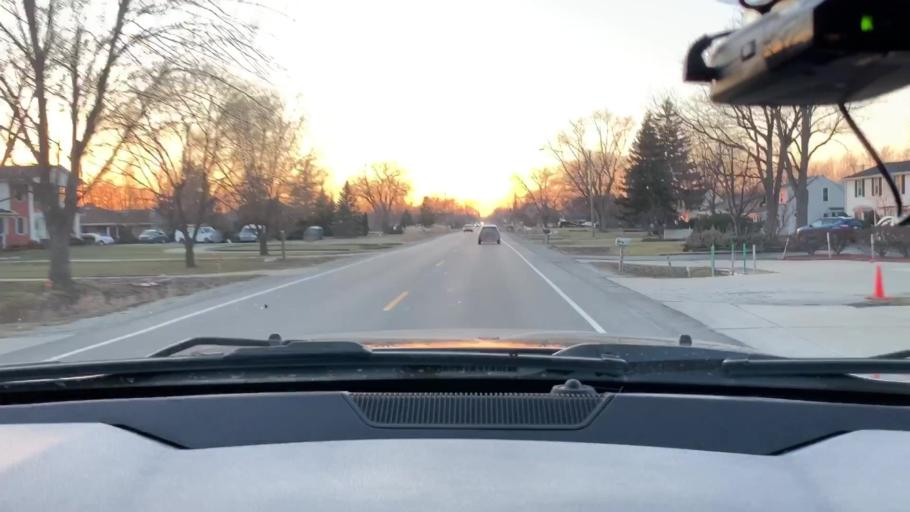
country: US
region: Michigan
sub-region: Wayne County
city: Flat Rock
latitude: 42.1237
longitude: -83.2810
